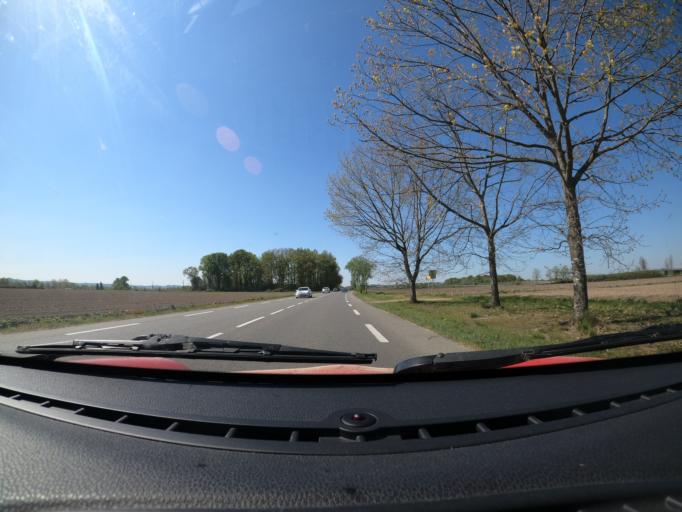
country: FR
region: Aquitaine
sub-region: Departement des Pyrenees-Atlantiques
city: Lescar
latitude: 43.3421
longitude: -0.4102
